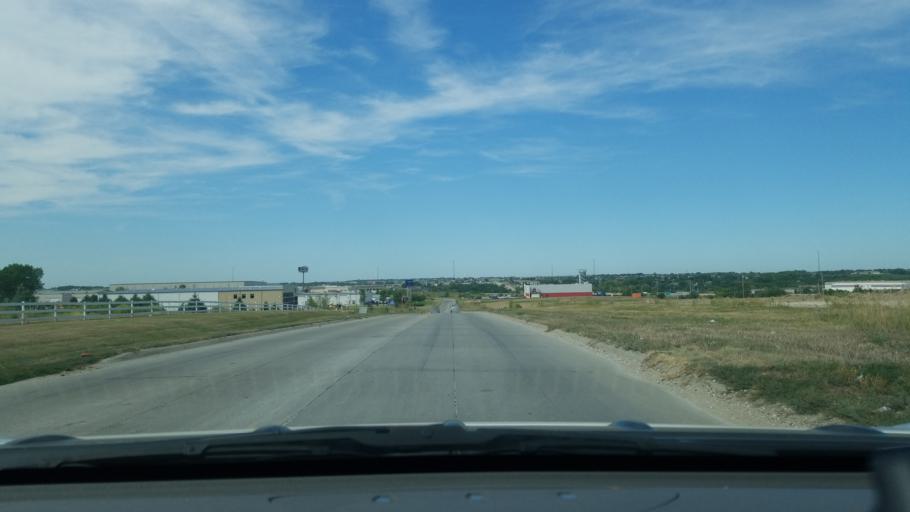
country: US
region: Nebraska
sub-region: Sarpy County
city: Chalco
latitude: 41.1455
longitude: -96.1501
